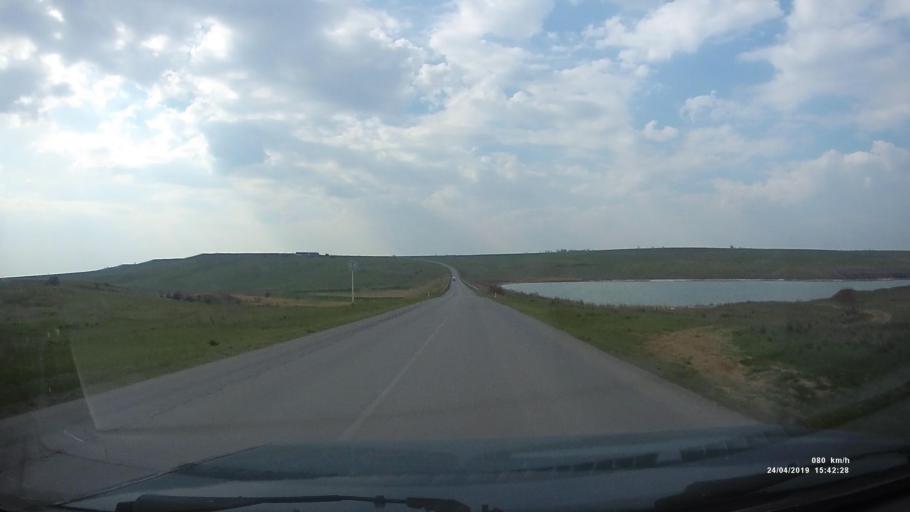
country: RU
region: Kalmykiya
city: Yashalta
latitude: 46.5763
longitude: 42.7876
